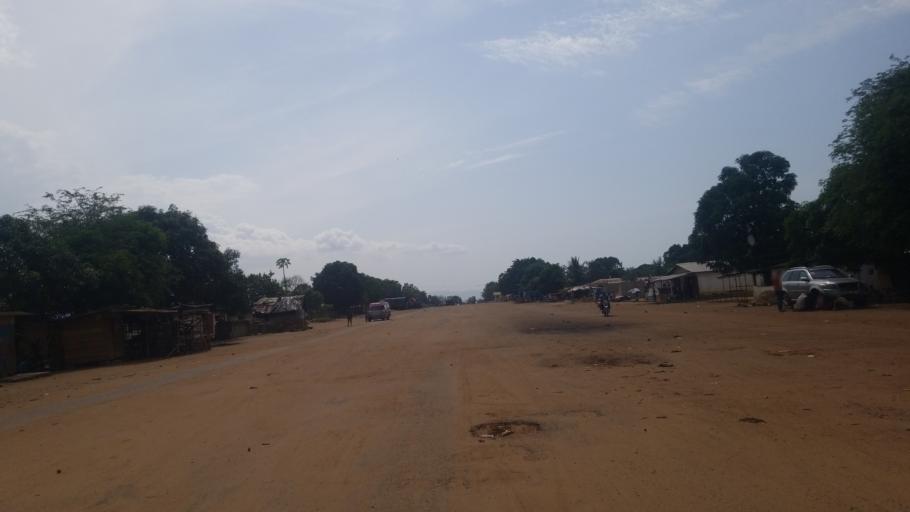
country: SL
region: Western Area
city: Waterloo
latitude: 8.3390
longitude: -13.0459
